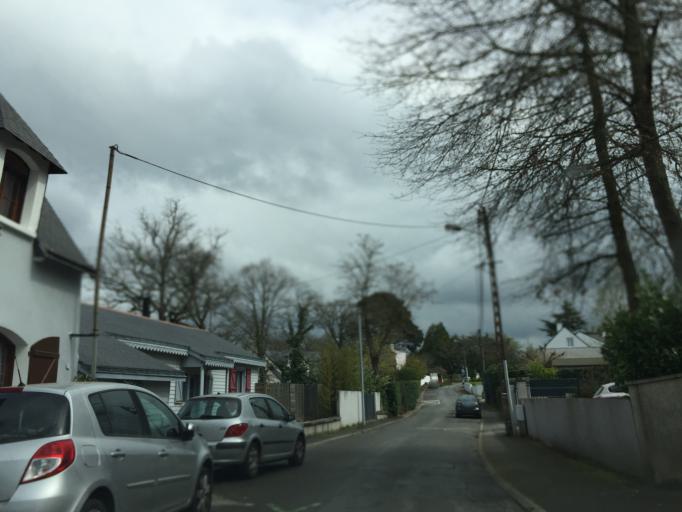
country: FR
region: Pays de la Loire
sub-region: Departement de la Loire-Atlantique
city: Suce-sur-Erdre
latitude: 47.3374
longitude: -1.5223
